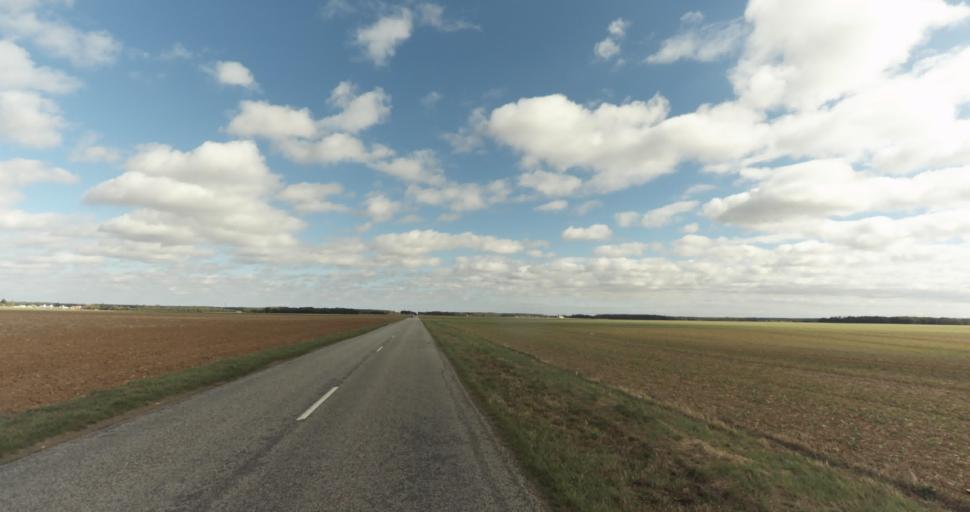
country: FR
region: Centre
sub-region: Departement d'Eure-et-Loir
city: Garnay
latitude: 48.7065
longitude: 1.3011
